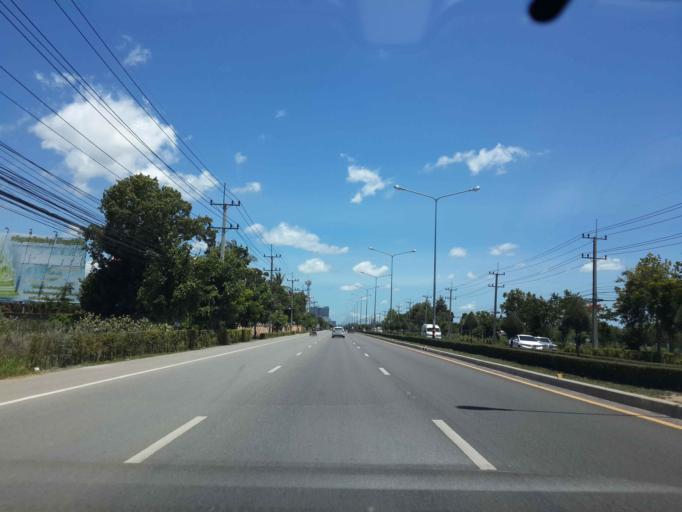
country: TH
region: Prachuap Khiri Khan
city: Hua Hin
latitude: 12.6823
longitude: 99.9527
